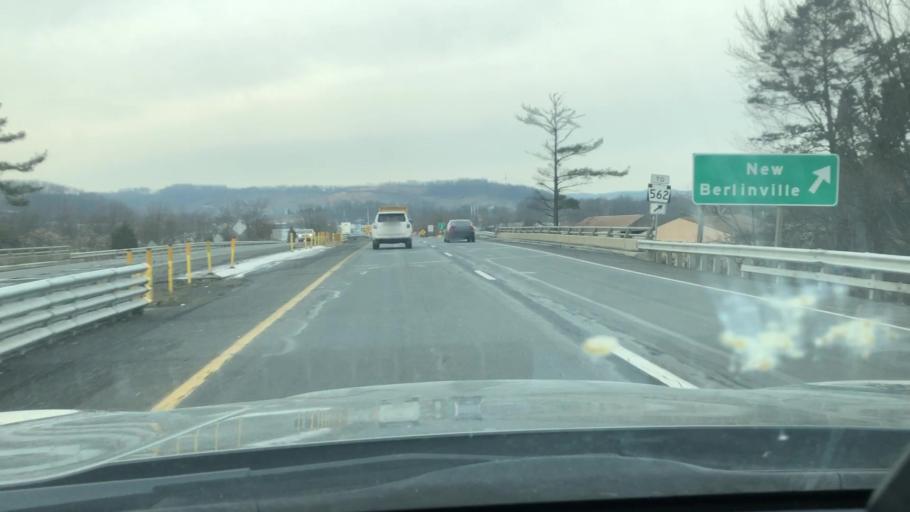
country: US
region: Pennsylvania
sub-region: Berks County
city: New Berlinville
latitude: 40.3461
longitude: -75.6247
